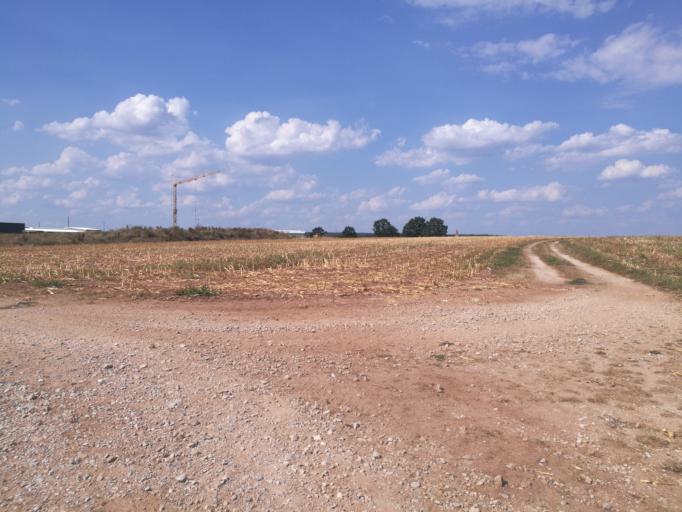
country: DE
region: Bavaria
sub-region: Regierungsbezirk Mittelfranken
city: Veitsbronn
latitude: 49.5016
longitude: 10.8839
